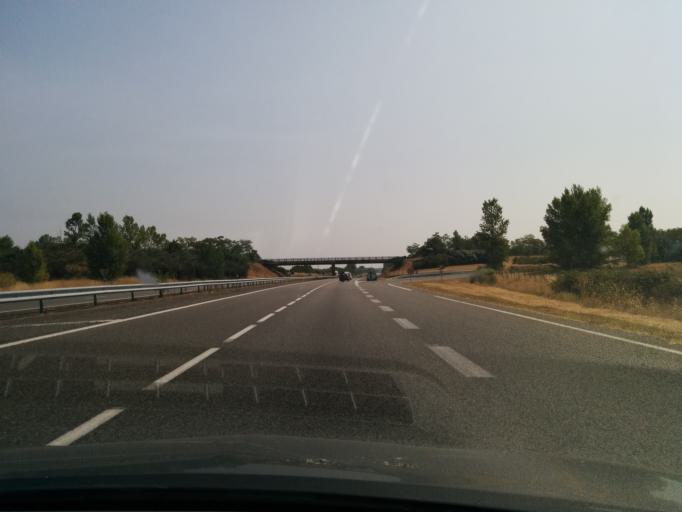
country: FR
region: Midi-Pyrenees
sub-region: Departement du Tarn
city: Lisle-sur-Tarn
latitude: 43.8401
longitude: 1.8431
